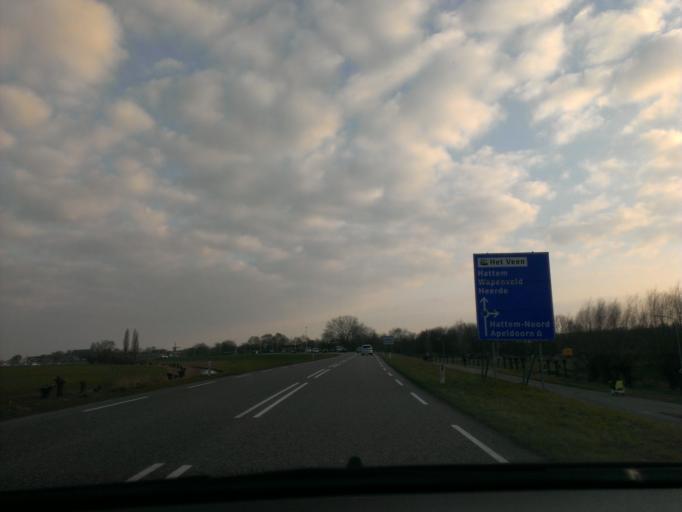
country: NL
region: Gelderland
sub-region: Gemeente Hattem
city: Hattem
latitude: 52.4848
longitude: 6.0602
